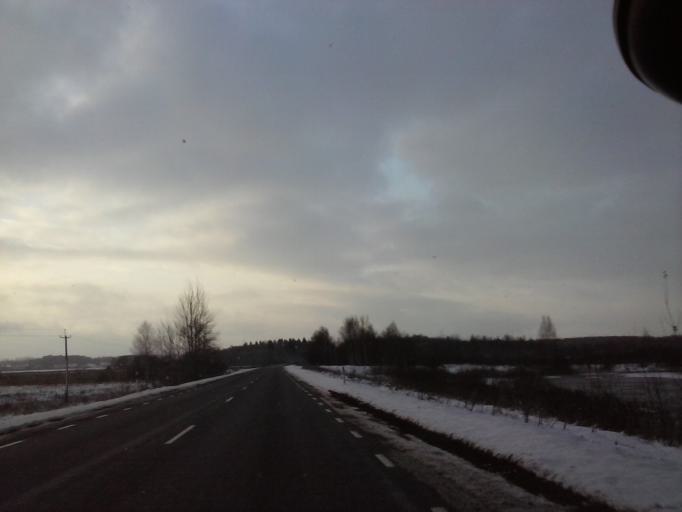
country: EE
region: Tartu
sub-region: UElenurme vald
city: Ulenurme
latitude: 58.3278
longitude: 26.7588
